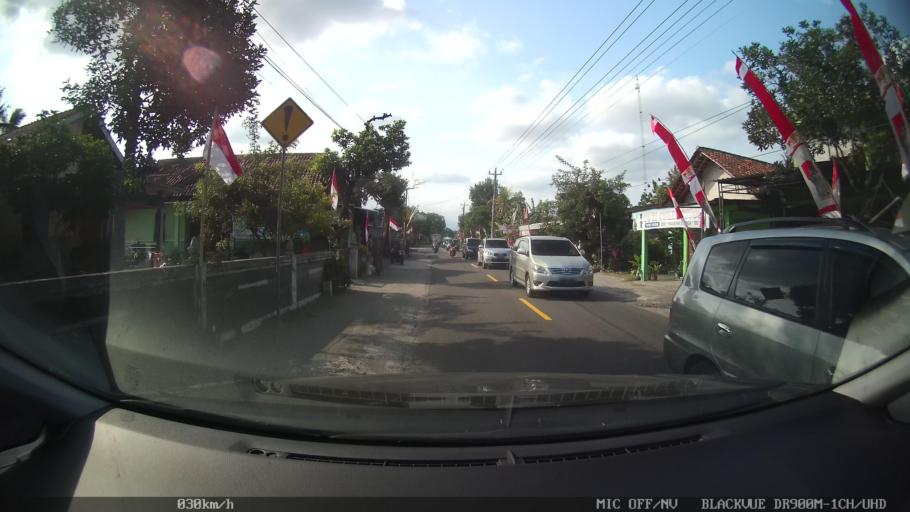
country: ID
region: Central Java
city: Candi Prambanan
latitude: -7.7259
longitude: 110.4725
